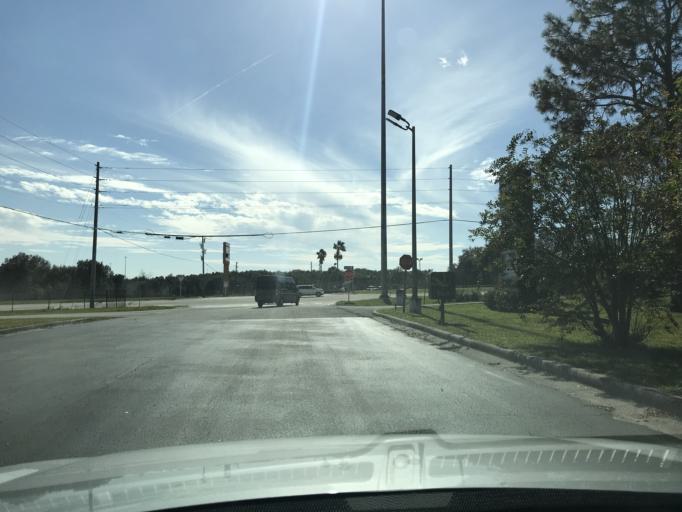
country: US
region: Florida
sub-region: Hernando County
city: Hill 'n Dale
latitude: 28.5240
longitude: -82.2396
